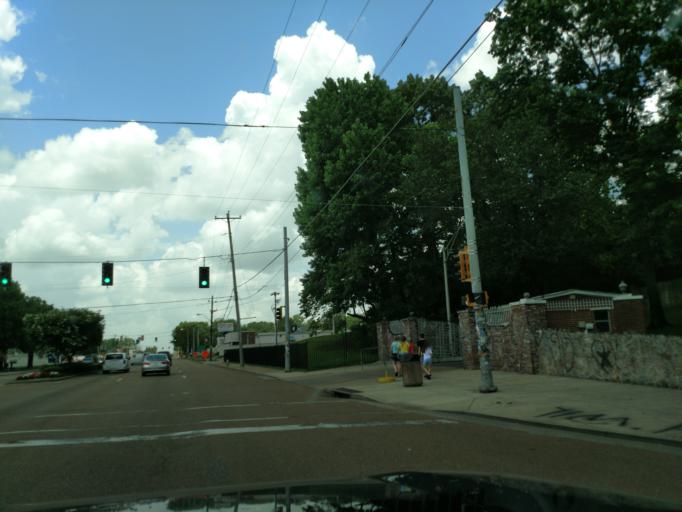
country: US
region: Tennessee
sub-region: Shelby County
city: New South Memphis
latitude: 35.0462
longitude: -90.0250
